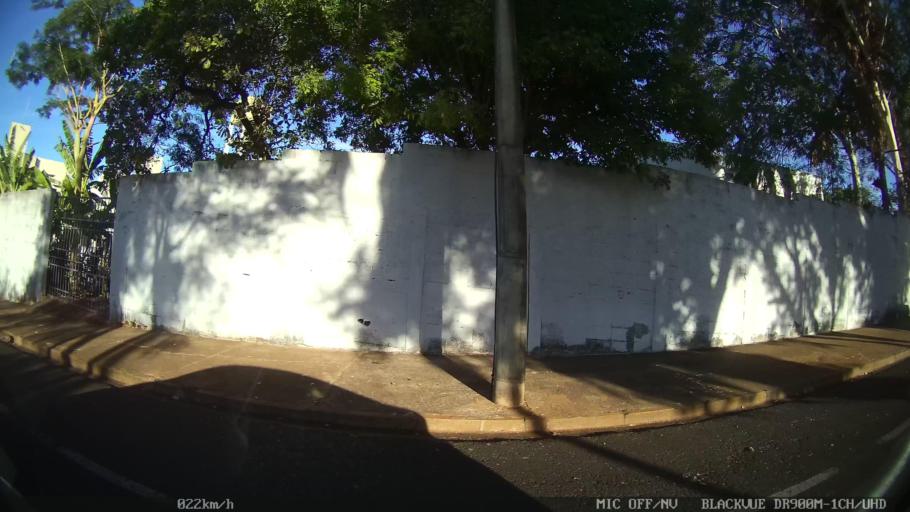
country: BR
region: Sao Paulo
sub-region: Sao Jose Do Rio Preto
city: Sao Jose do Rio Preto
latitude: -20.8301
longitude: -49.3678
